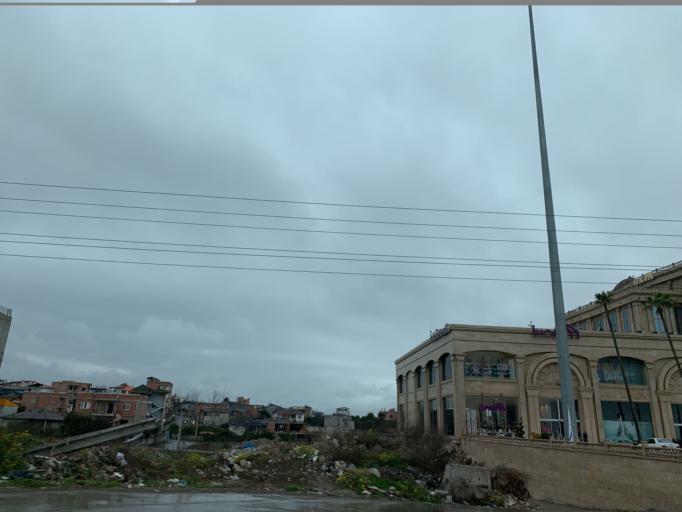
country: IR
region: Mazandaran
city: Amol
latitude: 36.4097
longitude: 52.3483
